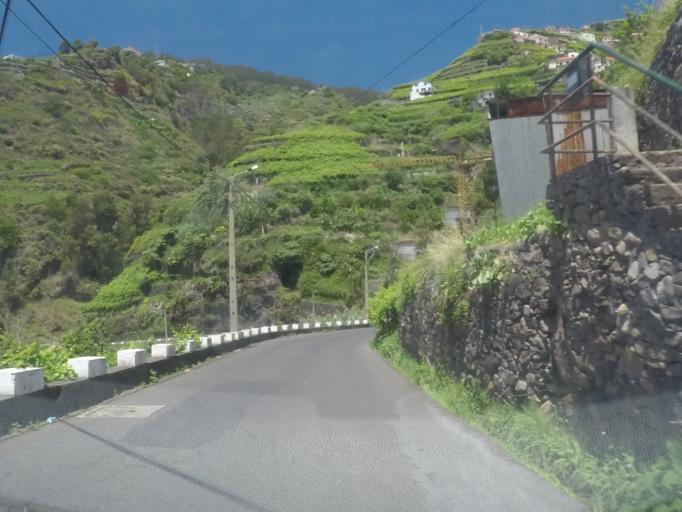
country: PT
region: Madeira
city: Camara de Lobos
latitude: 32.6718
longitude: -16.9850
